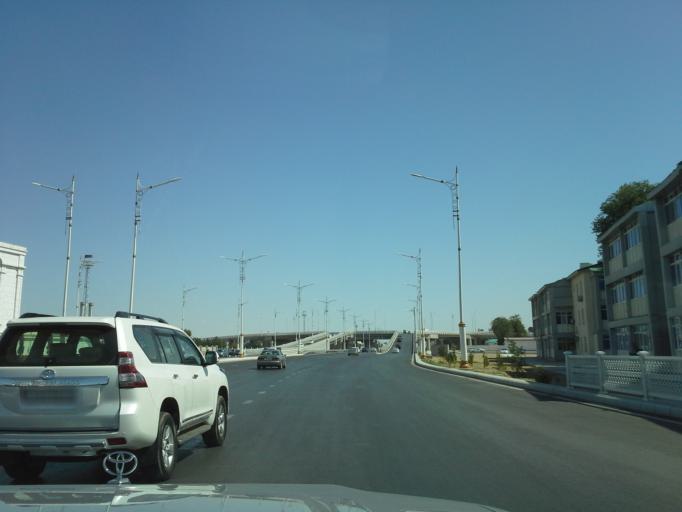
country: TM
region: Ahal
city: Ashgabat
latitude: 37.9420
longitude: 58.3966
